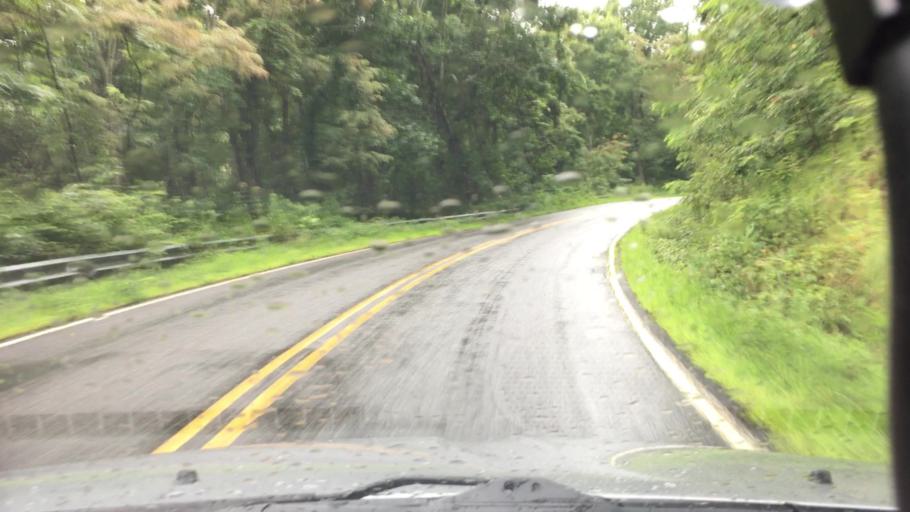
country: US
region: North Carolina
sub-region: Madison County
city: Mars Hill
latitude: 35.9136
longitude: -82.4825
